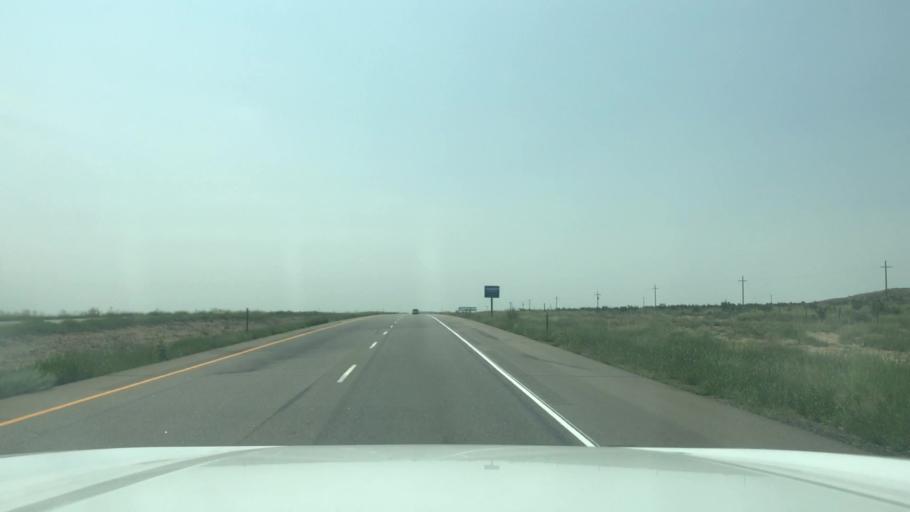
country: US
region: Colorado
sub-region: Pueblo County
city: Pueblo West
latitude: 38.3732
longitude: -104.6201
